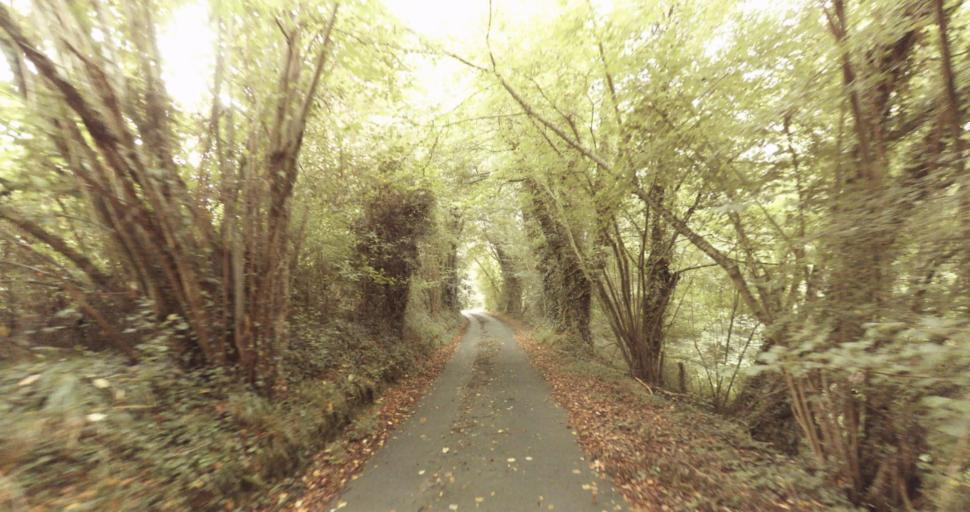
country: FR
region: Lower Normandy
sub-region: Departement de l'Orne
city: Vimoutiers
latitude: 48.9047
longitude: 0.1963
